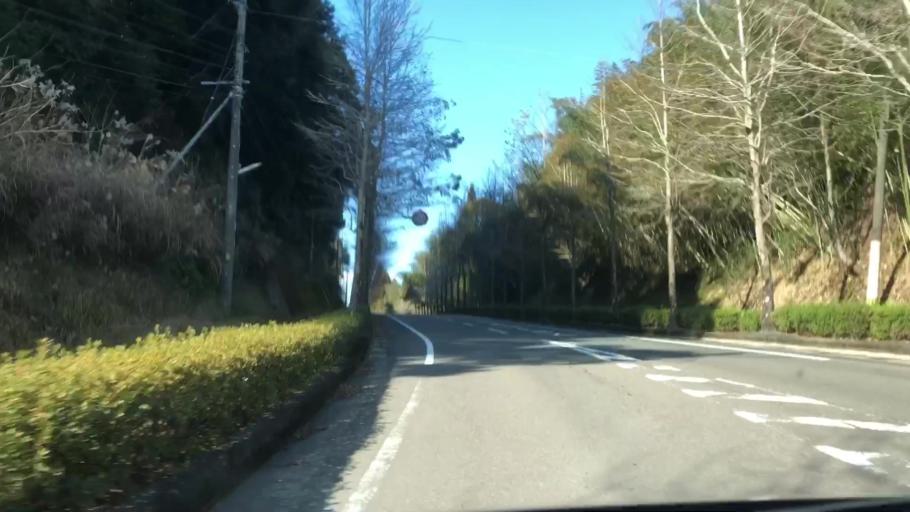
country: JP
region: Kagoshima
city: Satsumasendai
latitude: 31.8284
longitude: 130.4353
